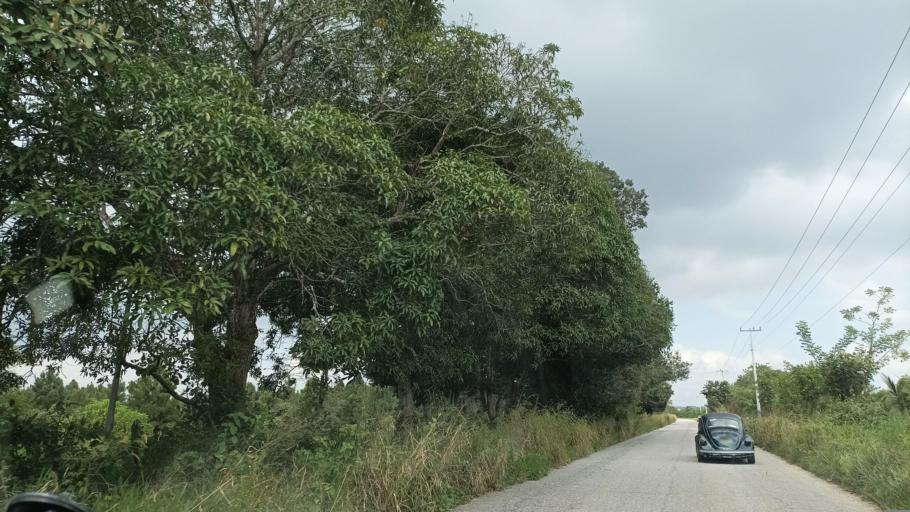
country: MX
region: Veracruz
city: Las Choapas
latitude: 17.8255
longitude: -94.1078
